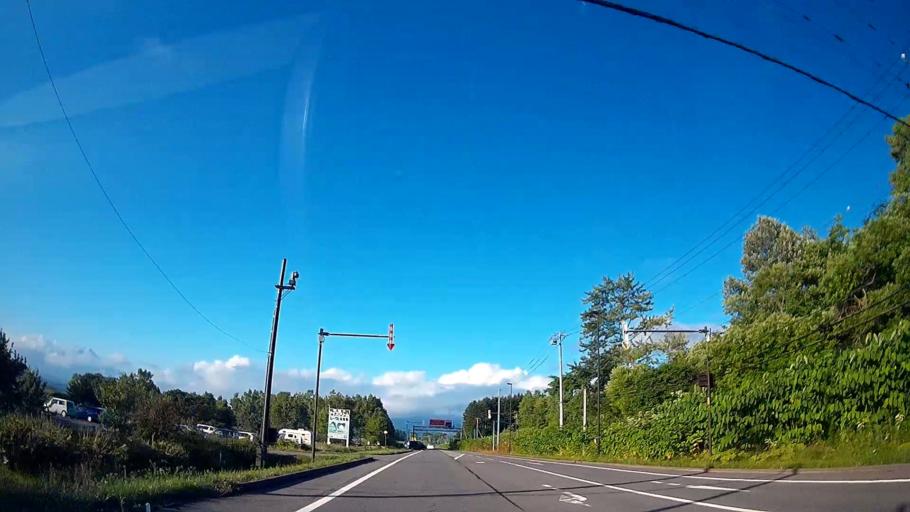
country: JP
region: Hokkaido
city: Date
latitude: 42.6146
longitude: 140.7866
